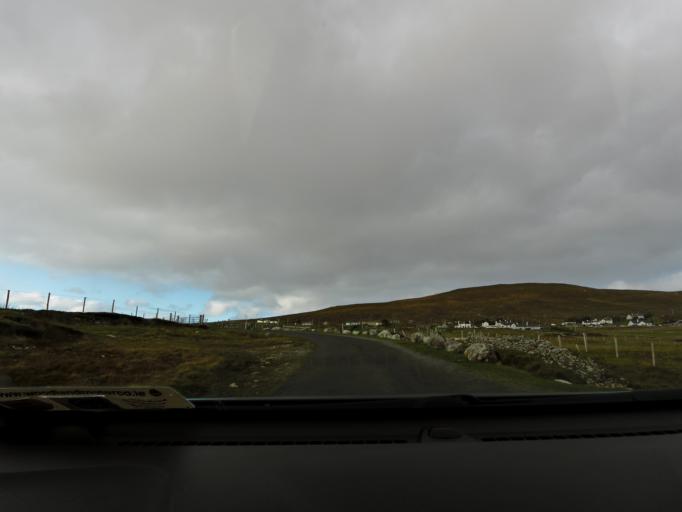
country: IE
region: Connaught
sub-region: Maigh Eo
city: Belmullet
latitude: 53.9033
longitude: -9.9905
